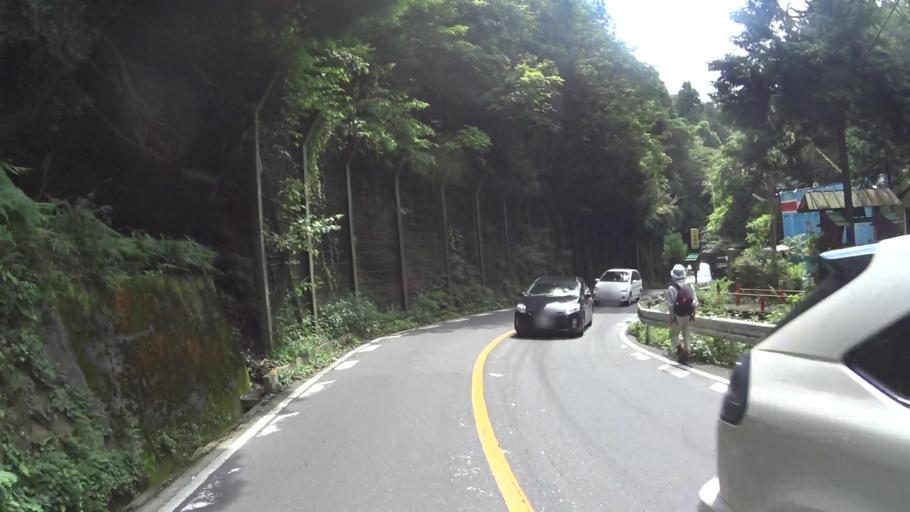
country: JP
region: Kyoto
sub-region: Kyoto-shi
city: Kamigyo-ku
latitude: 35.0369
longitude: 135.8090
